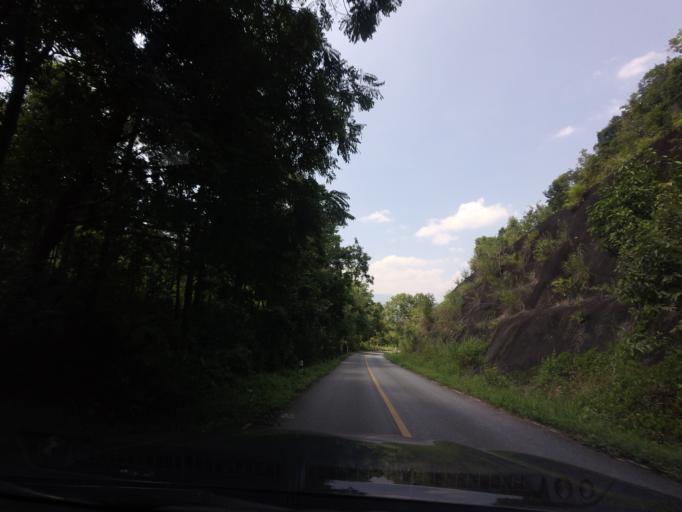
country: TH
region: Loei
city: Na Haeo
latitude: 17.6291
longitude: 100.9041
